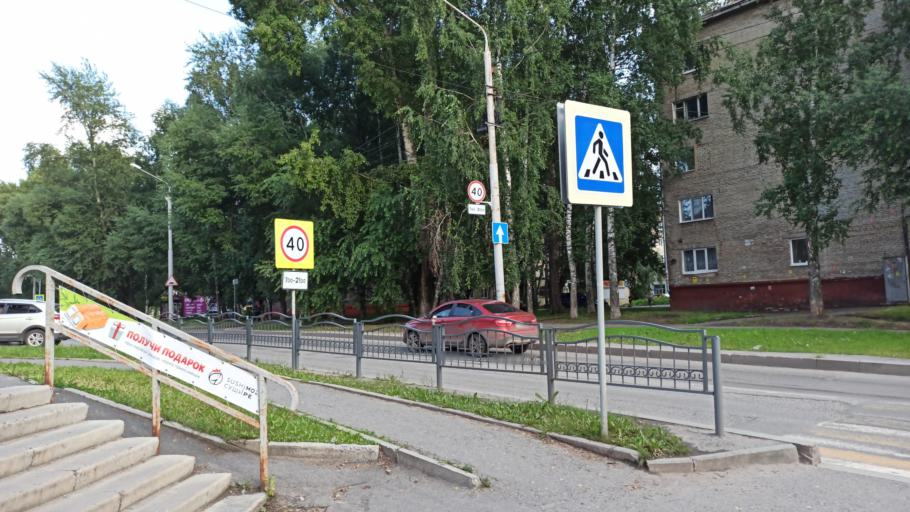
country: RU
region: Tomsk
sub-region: Tomskiy Rayon
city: Tomsk
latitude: 56.4808
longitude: 85.0032
